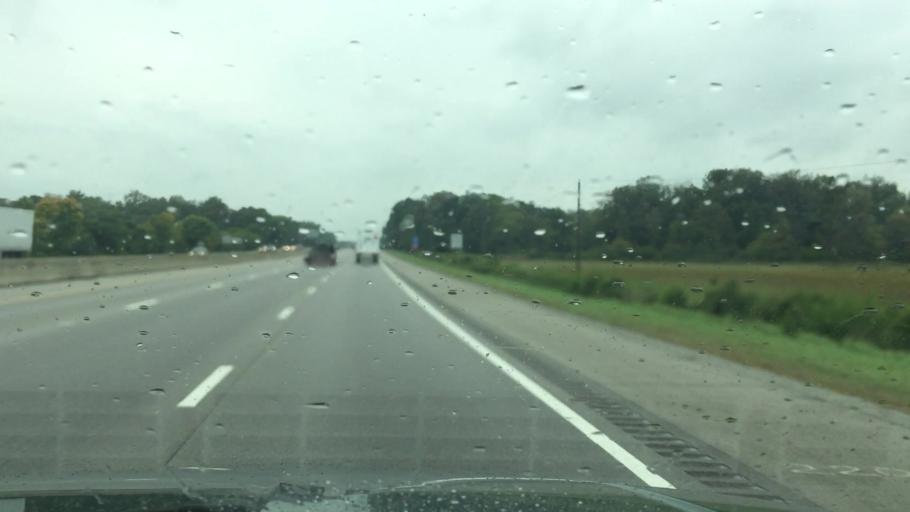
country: US
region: Ohio
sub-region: Clark County
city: Crystal Lakes
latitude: 39.8644
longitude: -84.0111
